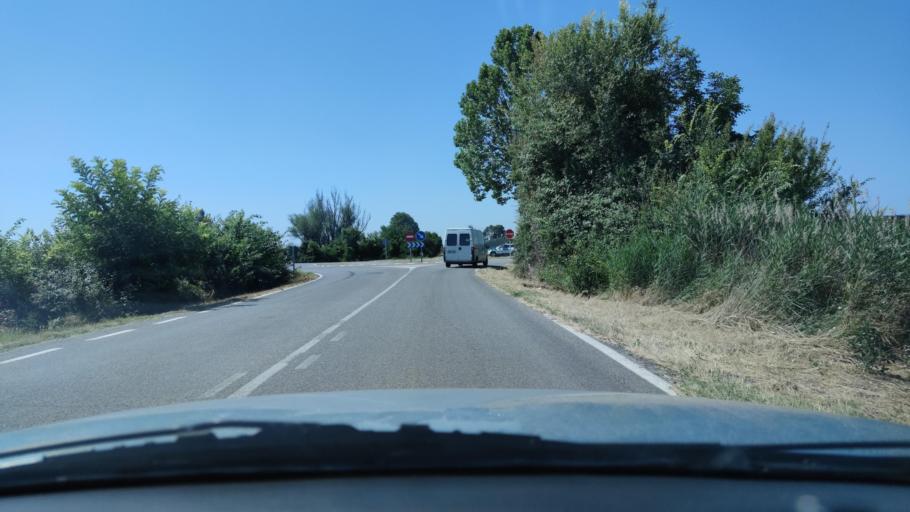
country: ES
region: Catalonia
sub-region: Provincia de Lleida
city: Penelles
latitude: 41.7300
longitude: 0.9829
